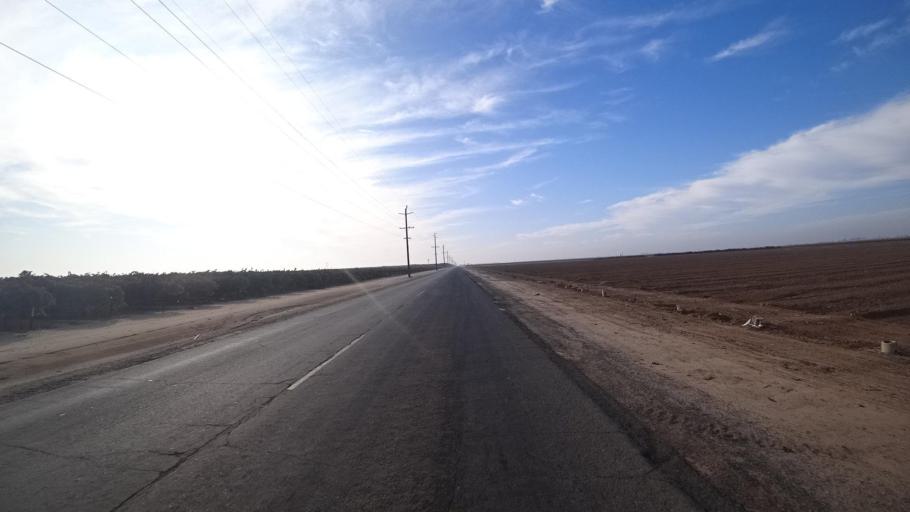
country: US
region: California
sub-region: Kern County
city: Delano
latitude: 35.7360
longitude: -119.2052
